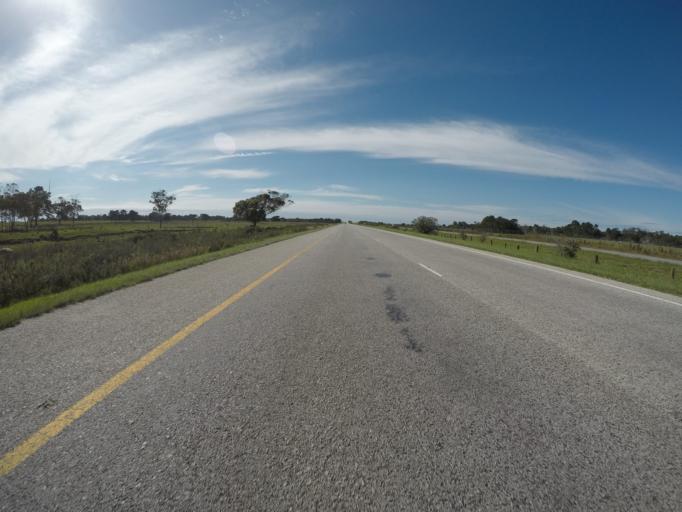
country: ZA
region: Eastern Cape
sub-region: Nelson Mandela Bay Metropolitan Municipality
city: Port Elizabeth
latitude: -33.9500
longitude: 25.4317
